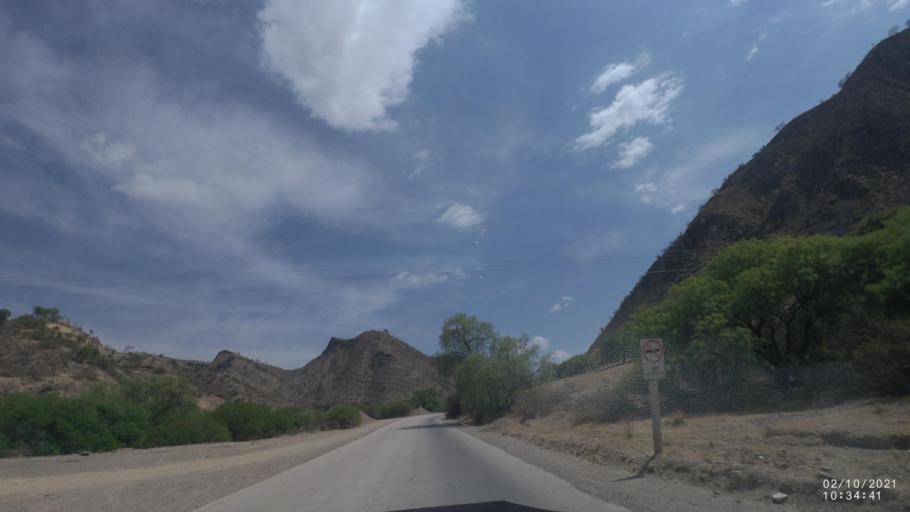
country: BO
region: Cochabamba
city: Capinota
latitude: -17.6707
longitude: -66.2565
